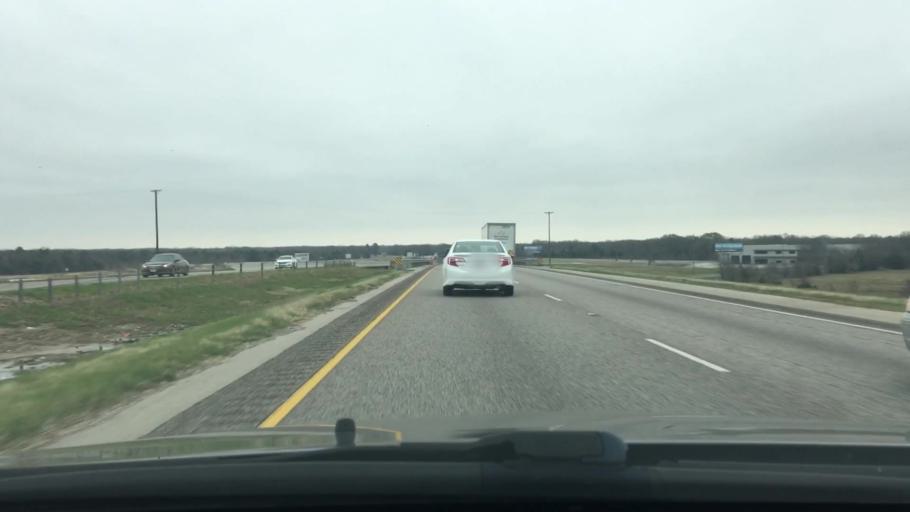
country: US
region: Texas
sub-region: Freestone County
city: Wortham
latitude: 31.8645
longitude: -96.3214
